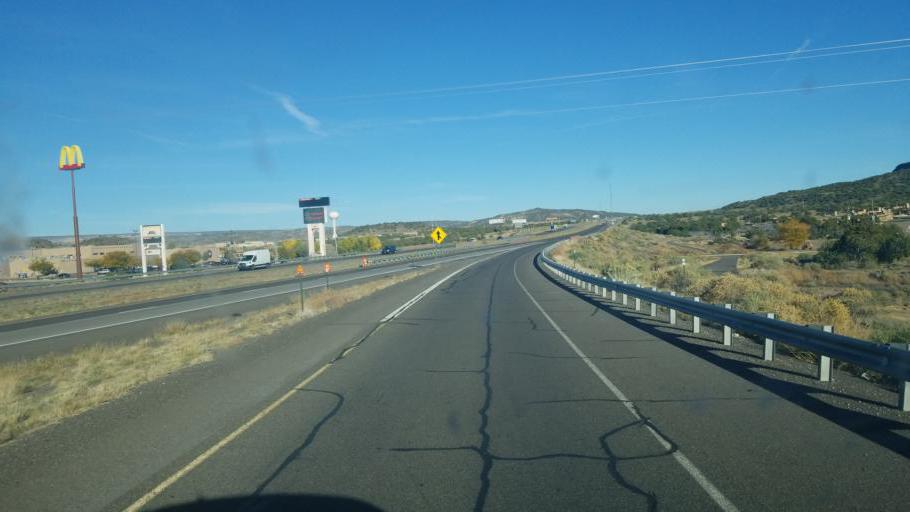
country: US
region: New Mexico
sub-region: Cibola County
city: Skyline-Ganipa
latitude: 35.0738
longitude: -107.5584
